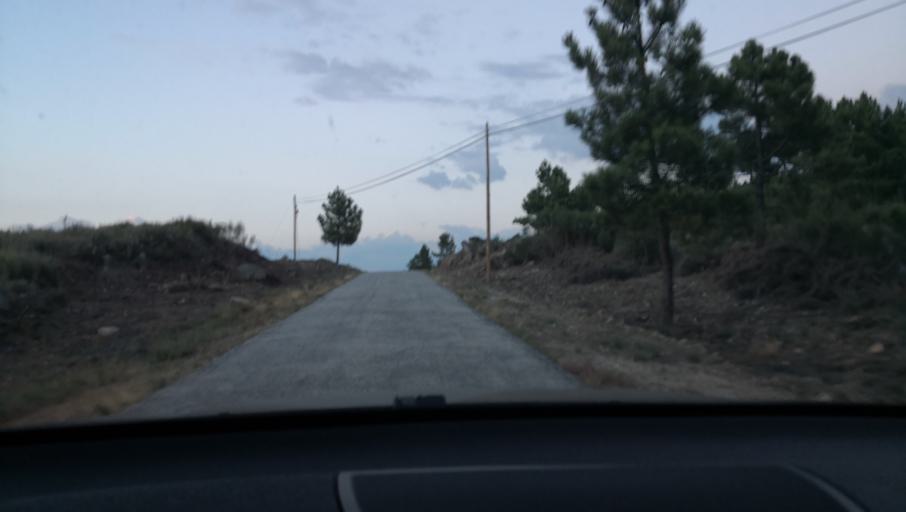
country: PT
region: Vila Real
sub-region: Sabrosa
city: Sabrosa
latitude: 41.2766
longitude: -7.6263
